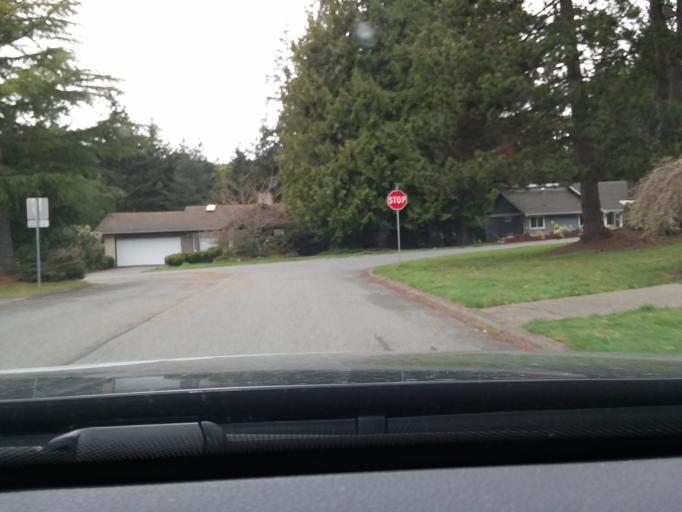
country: CA
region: British Columbia
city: North Saanich
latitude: 48.6166
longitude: -123.4271
